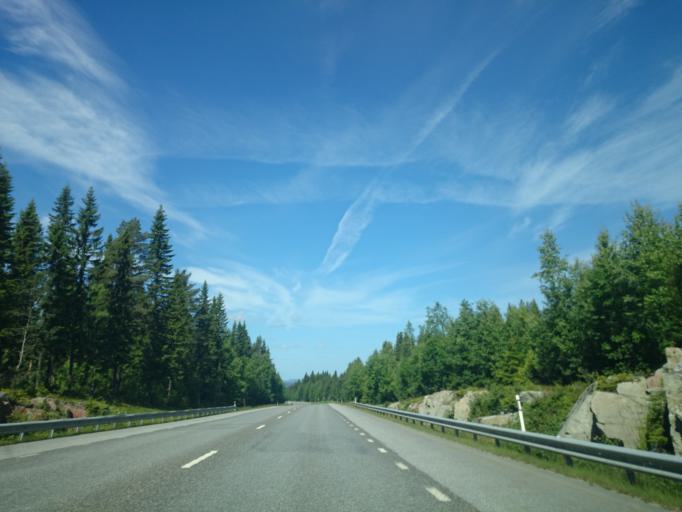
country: SE
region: Jaemtland
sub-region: Braecke Kommun
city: Braecke
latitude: 62.7025
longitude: 15.5074
